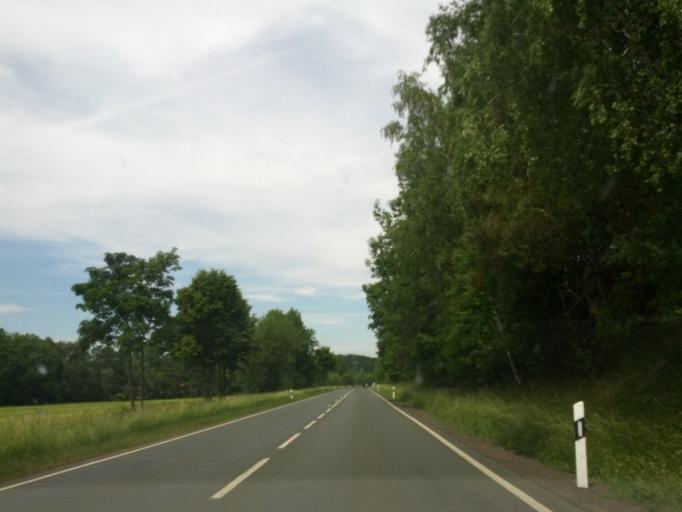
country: DE
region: Thuringia
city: Tabarz
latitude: 50.8905
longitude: 10.5182
